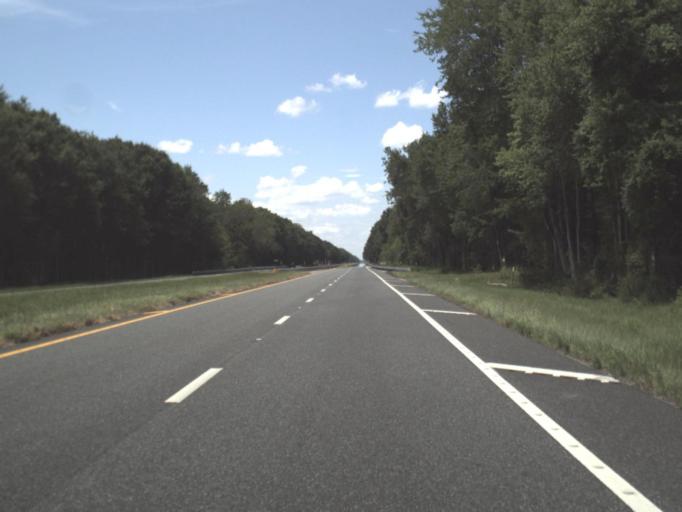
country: US
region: Florida
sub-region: Taylor County
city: Perry
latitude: 30.2493
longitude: -83.6991
